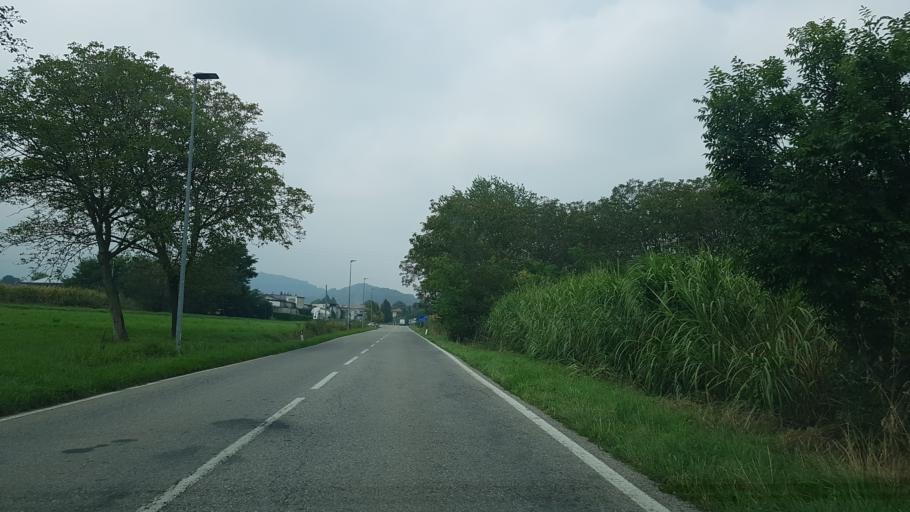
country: IT
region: Piedmont
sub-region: Provincia di Cuneo
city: Peveragno
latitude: 44.3304
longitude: 7.6302
